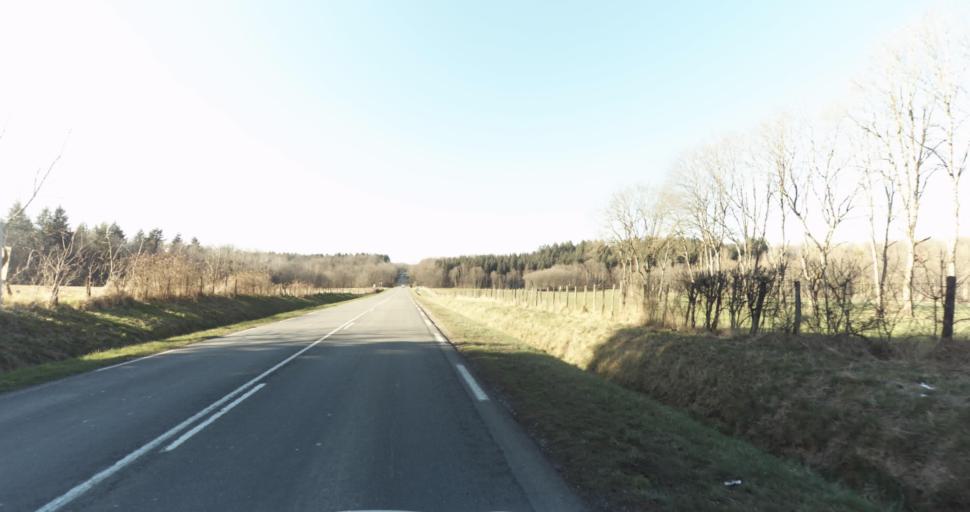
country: FR
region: Franche-Comte
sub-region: Departement du Jura
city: Montmorot
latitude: 46.6938
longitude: 5.4957
